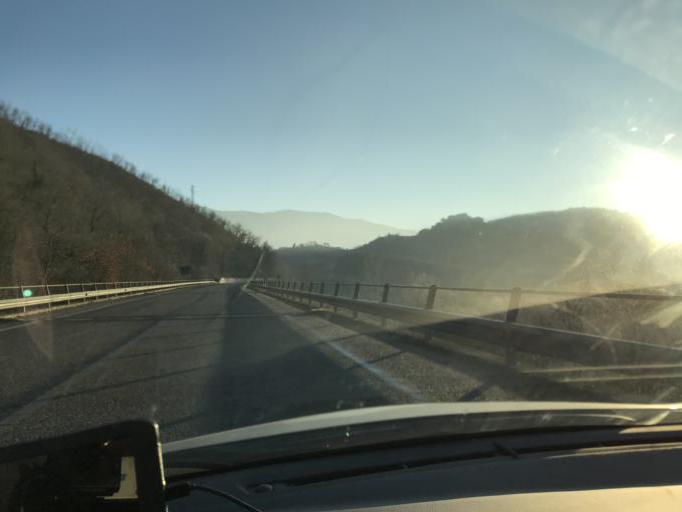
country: IT
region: Latium
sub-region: Provincia di Rieti
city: Concerviano
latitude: 42.3318
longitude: 12.9848
